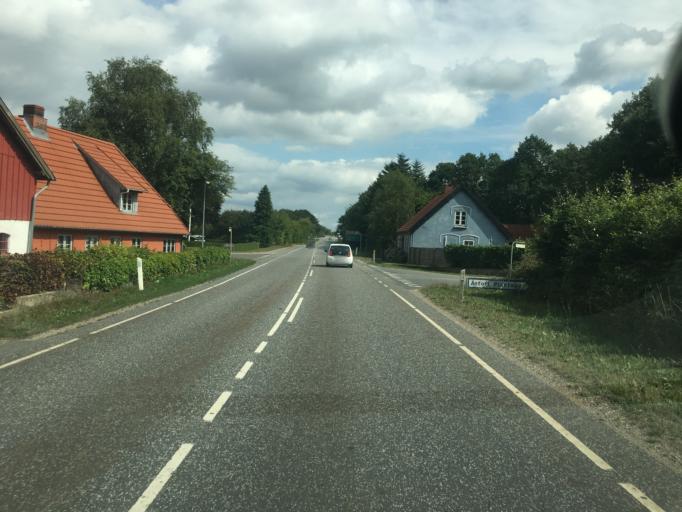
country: DK
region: South Denmark
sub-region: Aabenraa Kommune
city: Aabenraa
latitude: 54.9813
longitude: 9.3729
